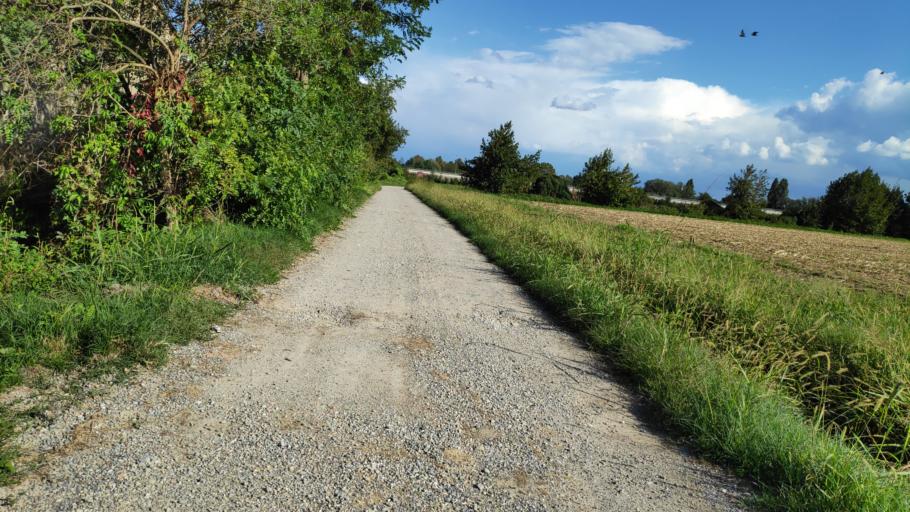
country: IT
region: Lombardy
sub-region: Citta metropolitana di Milano
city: Melzo
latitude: 45.4963
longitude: 9.4409
